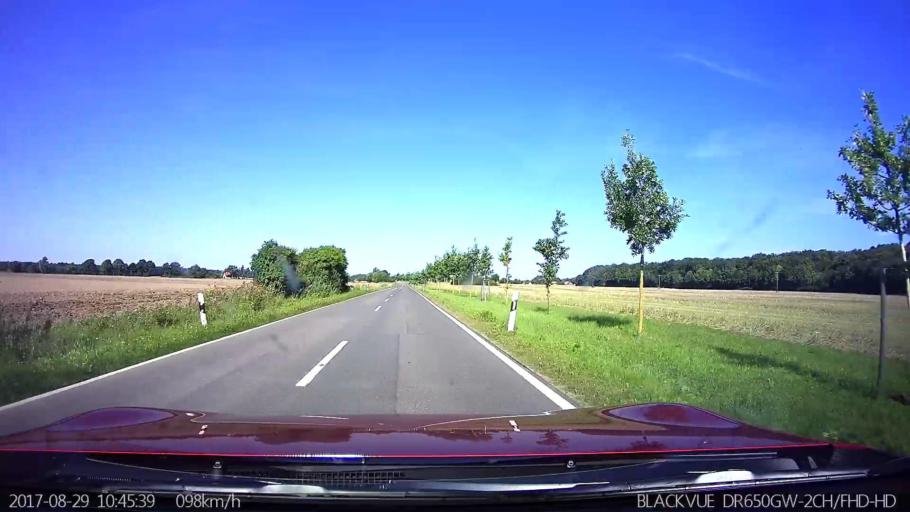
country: DE
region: Mecklenburg-Vorpommern
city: Richtenberg
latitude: 54.2154
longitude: 12.8582
